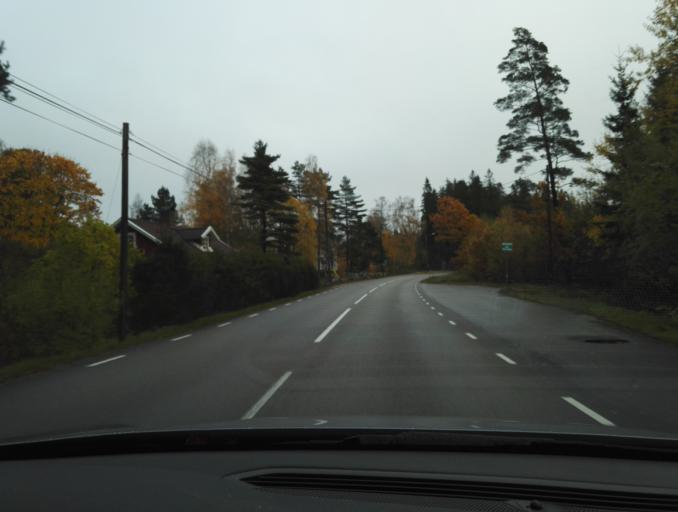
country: SE
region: Kronoberg
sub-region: Vaxjo Kommun
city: Rottne
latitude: 57.0338
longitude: 14.7967
